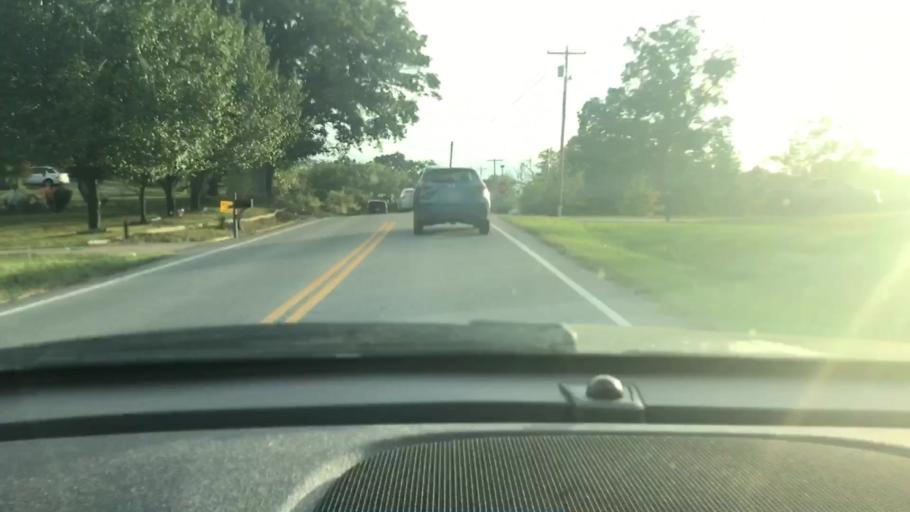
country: US
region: Tennessee
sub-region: Dickson County
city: Charlotte
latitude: 36.2645
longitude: -87.2178
